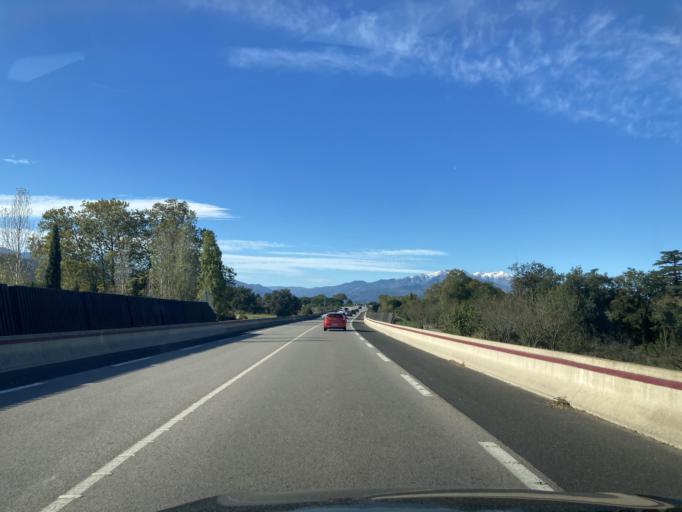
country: FR
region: Languedoc-Roussillon
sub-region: Departement des Pyrenees-Orientales
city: Montesquiu d'Albera
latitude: 42.5374
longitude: 2.8780
